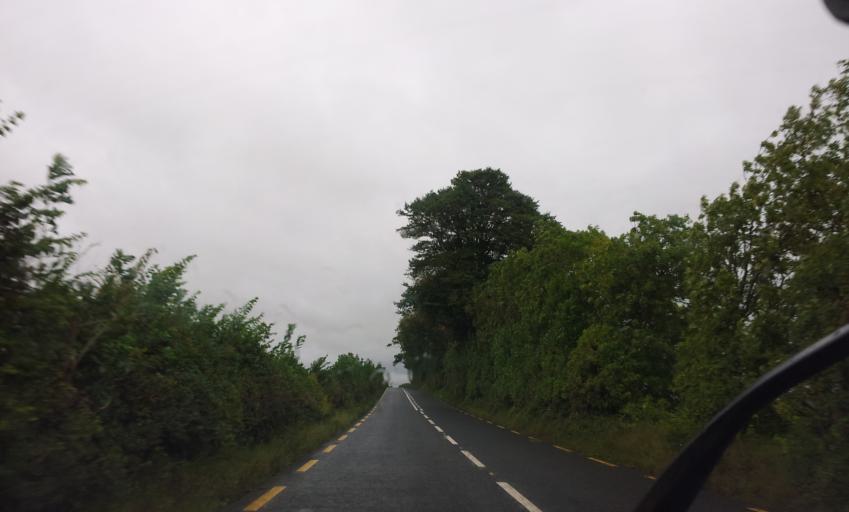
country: IE
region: Munster
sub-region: County Cork
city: Mitchelstown
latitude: 52.2629
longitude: -8.3105
